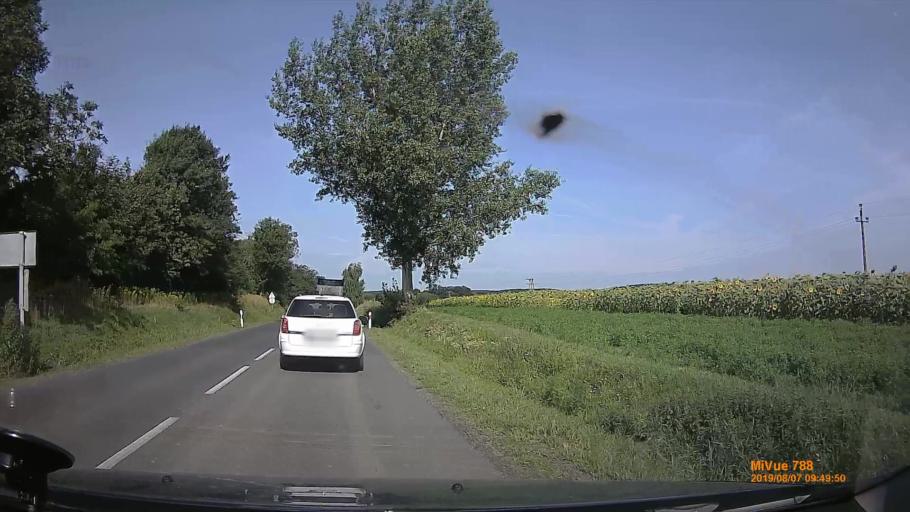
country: HU
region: Zala
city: Pacsa
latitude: 46.7414
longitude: 16.9293
